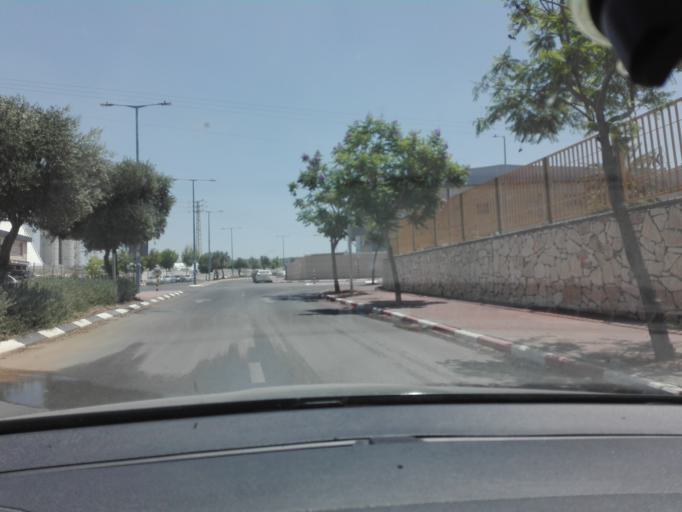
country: IL
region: Southern District
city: Qiryat Gat
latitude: 31.5943
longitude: 34.7788
